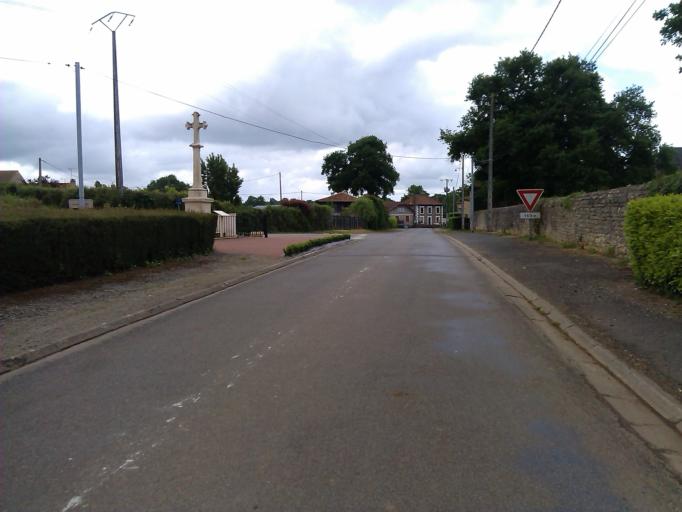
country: FR
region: Poitou-Charentes
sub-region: Departement de la Vienne
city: Charroux
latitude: 46.0914
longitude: 0.4984
